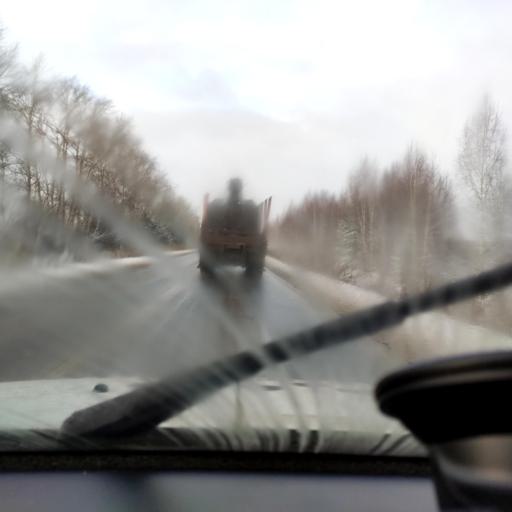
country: RU
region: Perm
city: Nytva
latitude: 57.9422
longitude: 55.3681
